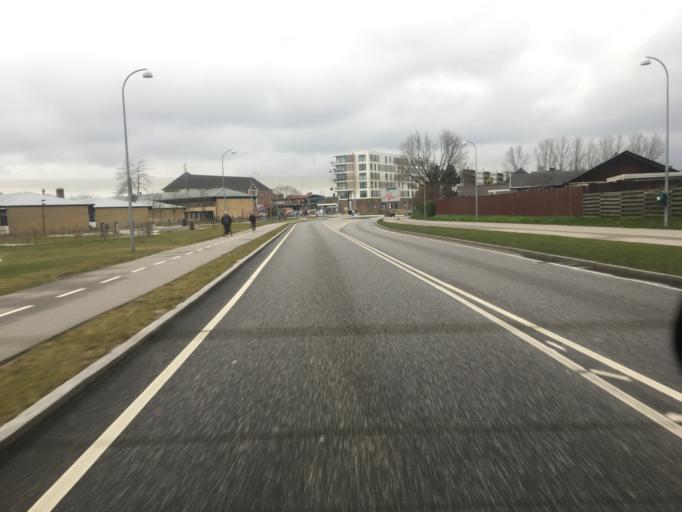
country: DK
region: Capital Region
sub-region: Vallensbaek Kommune
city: Vallensbaek
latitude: 55.6212
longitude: 12.3911
